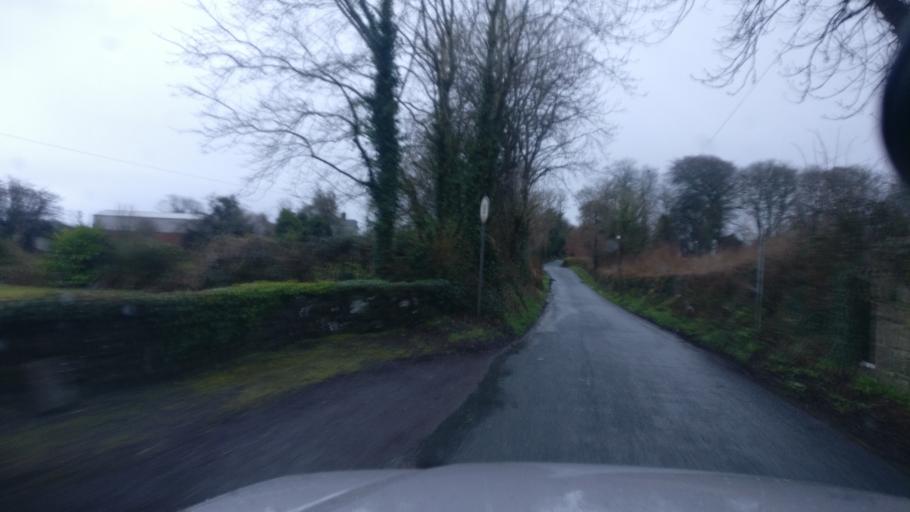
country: IE
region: Connaught
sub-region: County Galway
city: Ballinasloe
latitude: 53.3309
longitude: -8.3978
